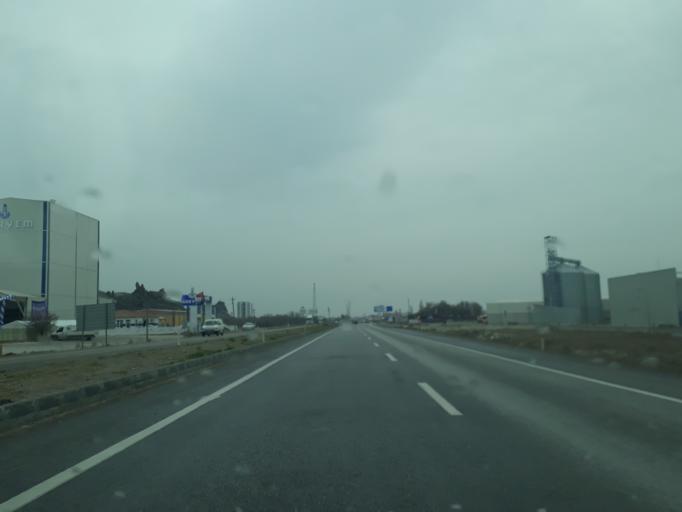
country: TR
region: Konya
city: Karapinar
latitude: 37.7144
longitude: 33.5864
